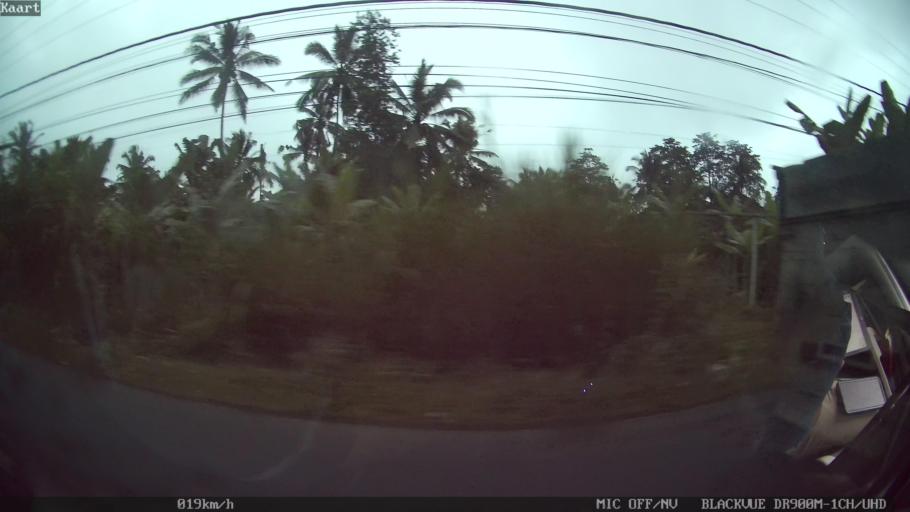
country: ID
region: Bali
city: Banjar Ponggang
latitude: -8.3909
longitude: 115.2594
